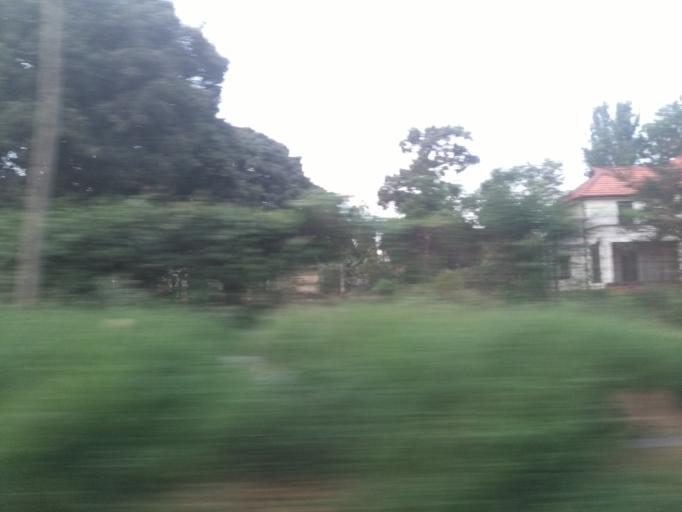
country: UG
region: Eastern Region
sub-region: Jinja District
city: Jinja
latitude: 0.4313
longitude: 33.1992
